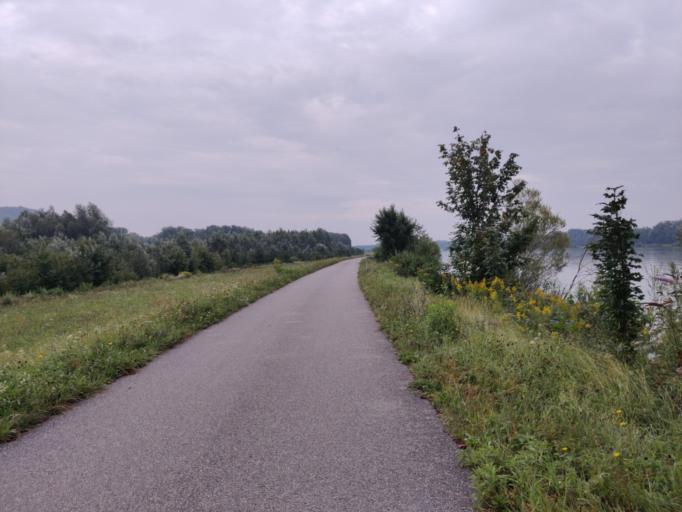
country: AT
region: Upper Austria
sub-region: Politischer Bezirk Urfahr-Umgebung
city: Steyregg
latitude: 48.2685
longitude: 14.3864
